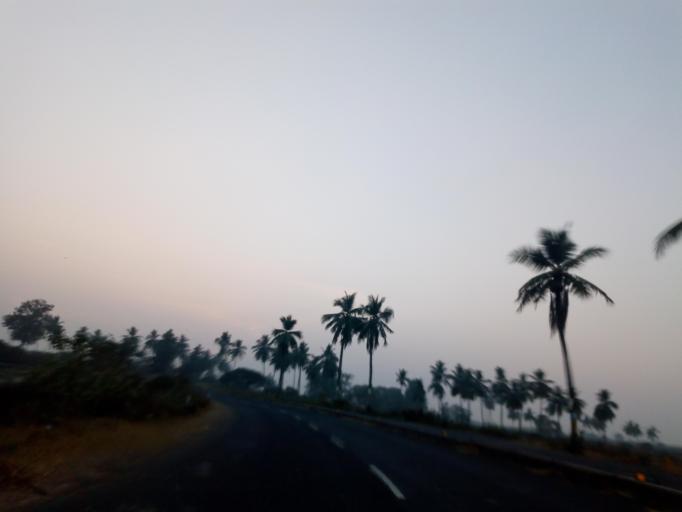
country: IN
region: Andhra Pradesh
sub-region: West Godavari
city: Tadepallegudem
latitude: 16.8234
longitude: 81.4721
